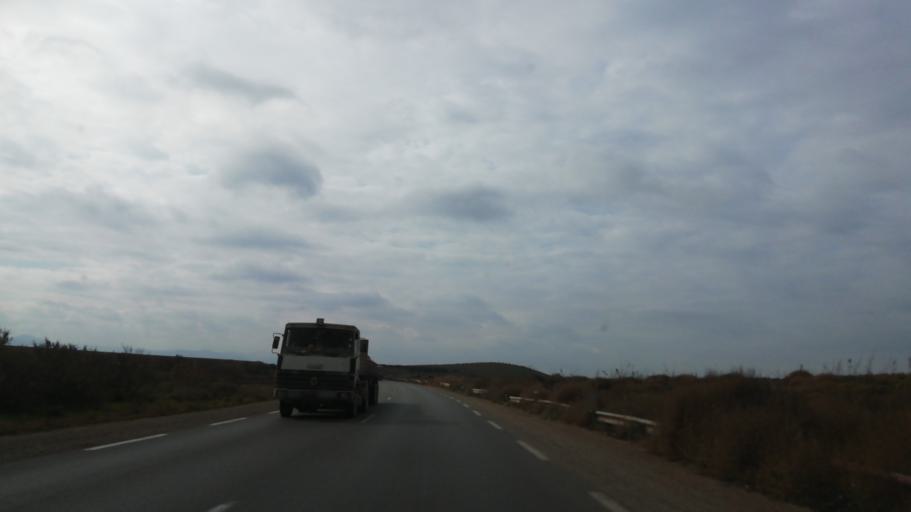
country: DZ
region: Oran
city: Sidi ech Chahmi
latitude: 35.5950
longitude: -0.4503
